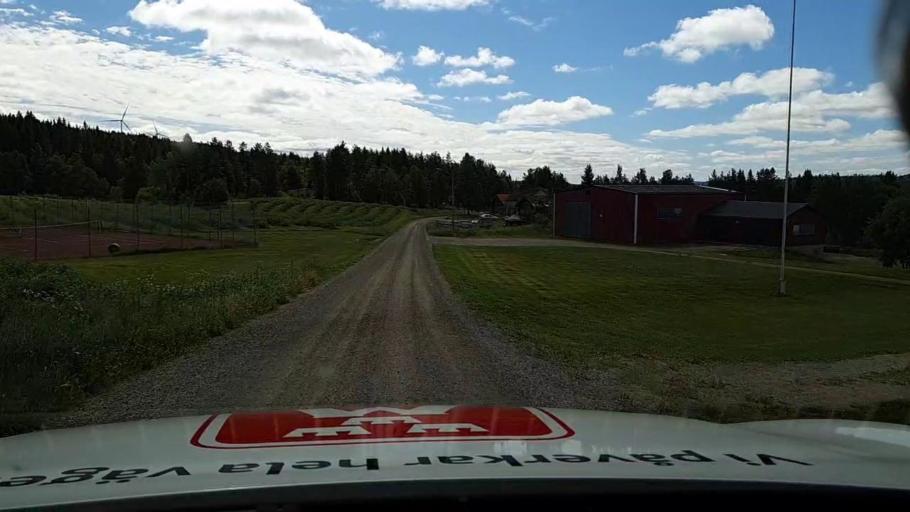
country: SE
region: Jaemtland
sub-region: Braecke Kommun
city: Braecke
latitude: 62.7642
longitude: 15.4985
